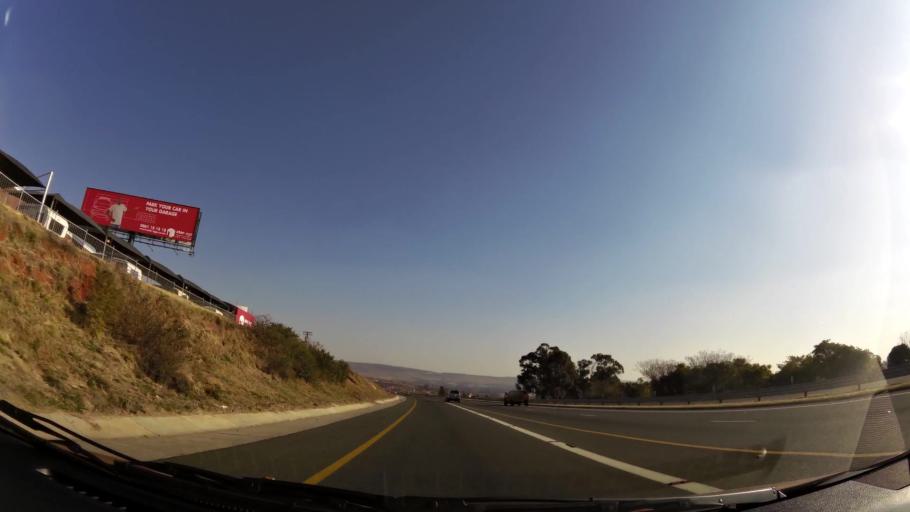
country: ZA
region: Gauteng
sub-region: West Rand District Municipality
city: Muldersdriseloop
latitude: -26.0242
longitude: 27.8527
